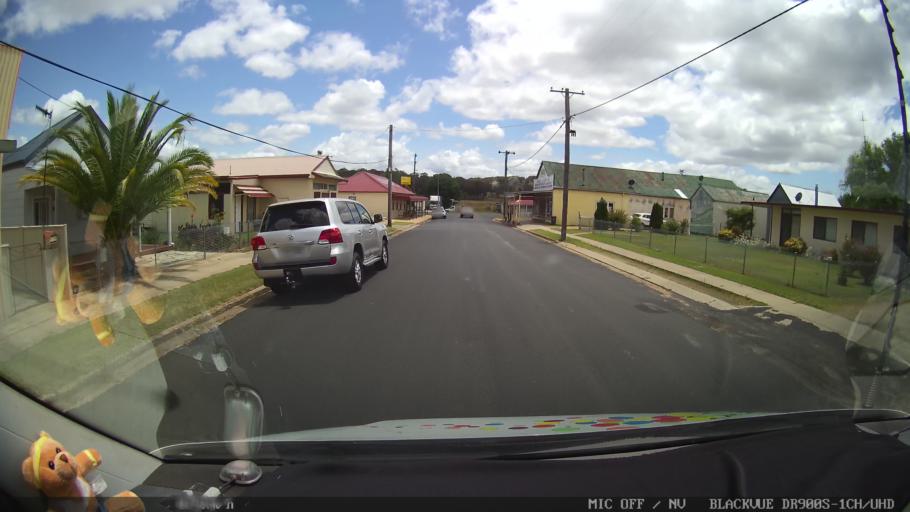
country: AU
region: New South Wales
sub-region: Glen Innes Severn
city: Glen Innes
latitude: -29.4436
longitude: 151.5993
